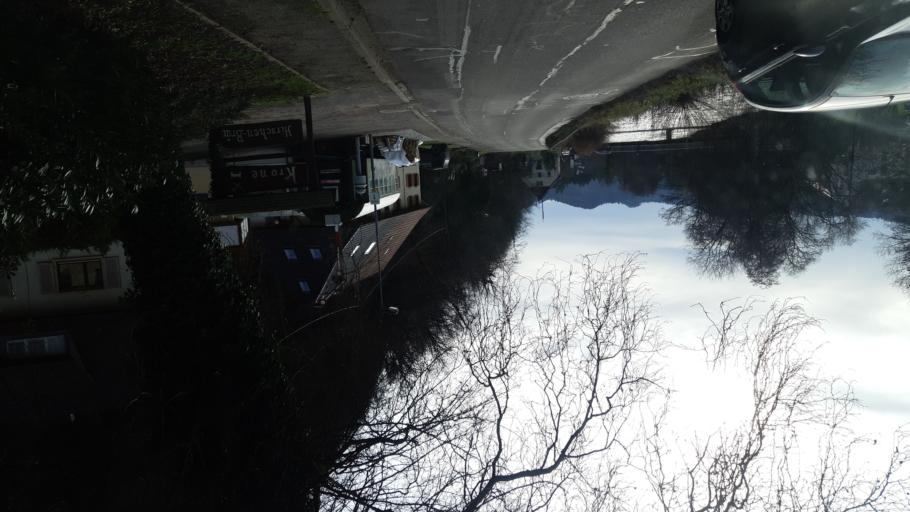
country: DE
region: Baden-Wuerttemberg
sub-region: Freiburg Region
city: Gutach im Breisgau
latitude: 48.1182
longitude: 7.9872
